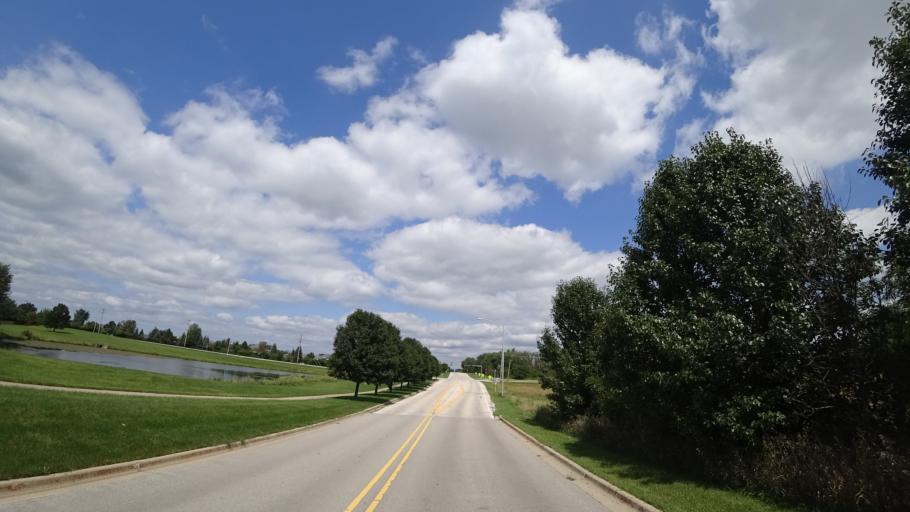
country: US
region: Illinois
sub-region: Cook County
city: Orland Hills
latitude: 41.5631
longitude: -87.8710
